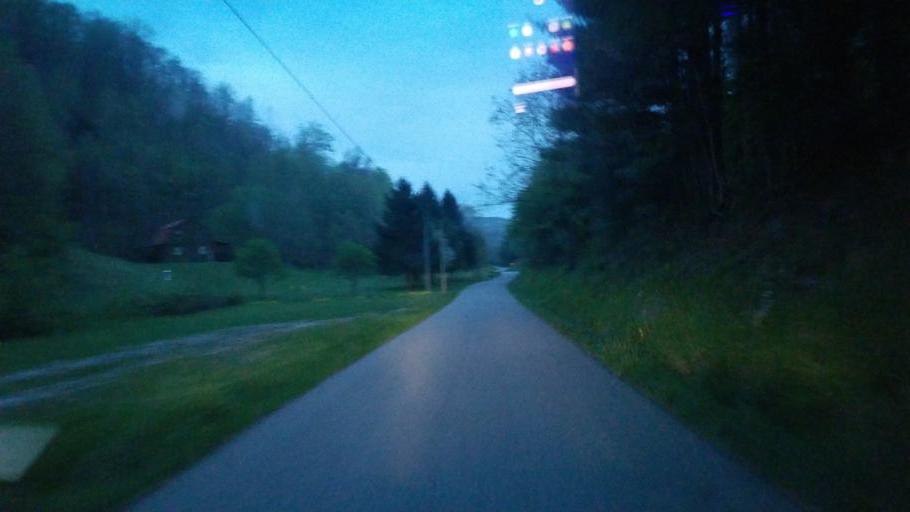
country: US
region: Virginia
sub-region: Smyth County
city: Marion
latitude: 36.8277
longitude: -81.4678
